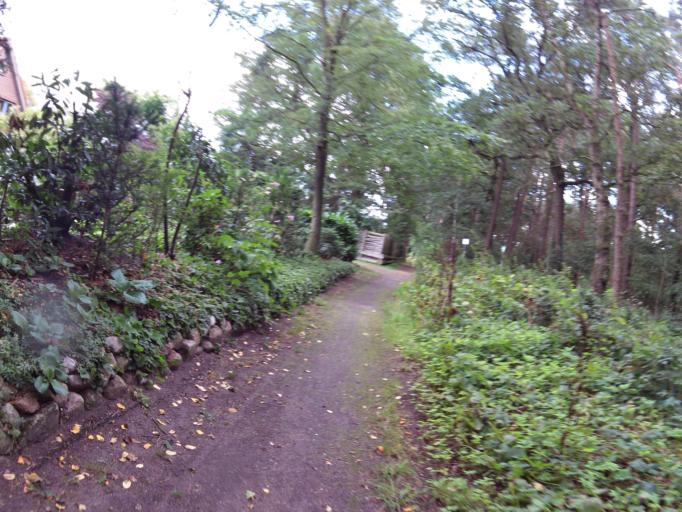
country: DE
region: Lower Saxony
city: Heeslingen
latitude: 53.3150
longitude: 9.3255
